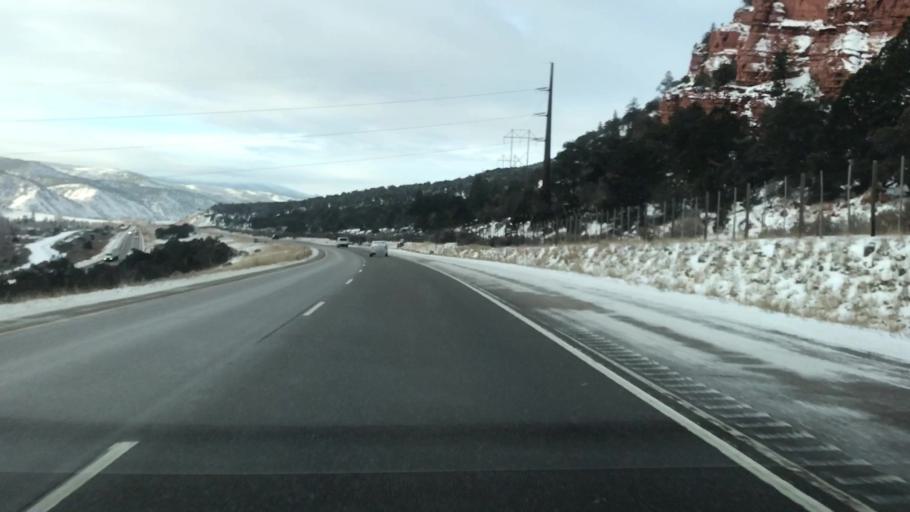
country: US
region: Colorado
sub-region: Eagle County
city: Eagle
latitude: 39.6958
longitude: -106.7434
